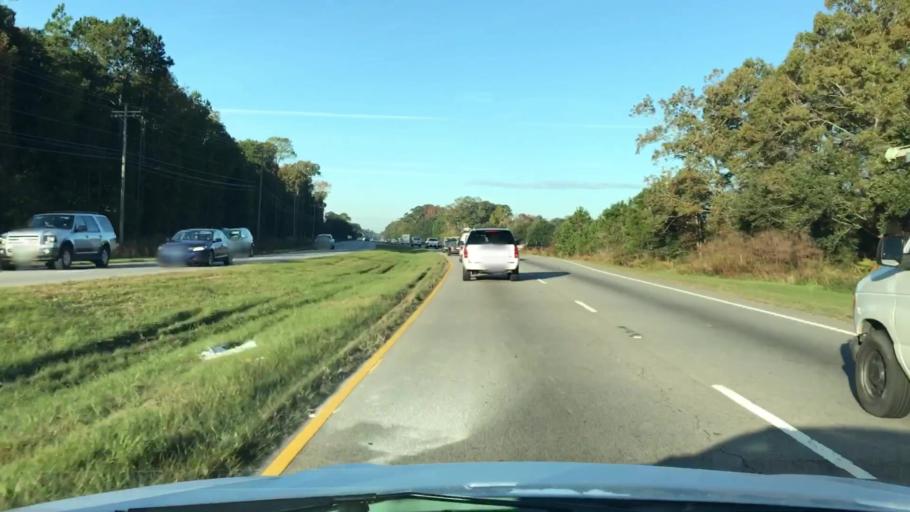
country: US
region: South Carolina
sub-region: Charleston County
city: Shell Point
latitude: 32.7942
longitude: -80.0590
